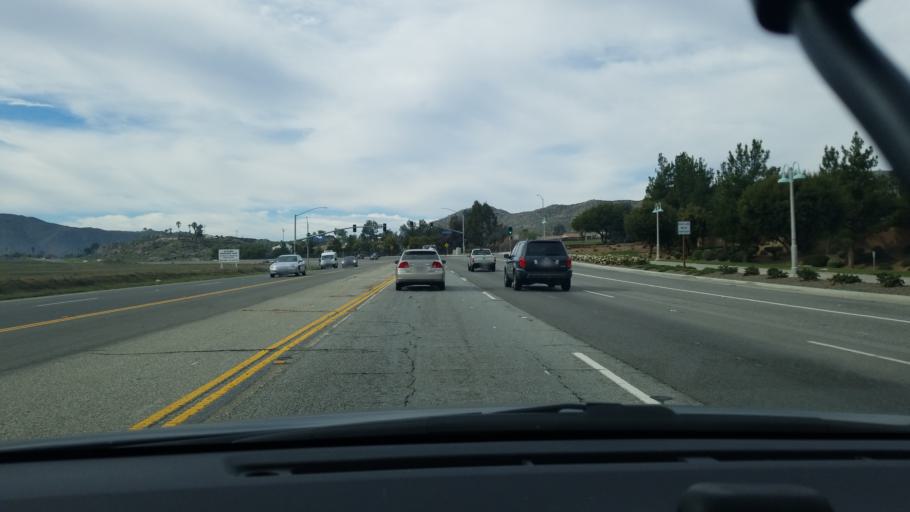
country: US
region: California
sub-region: Riverside County
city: Green Acres
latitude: 33.7439
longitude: -117.0586
